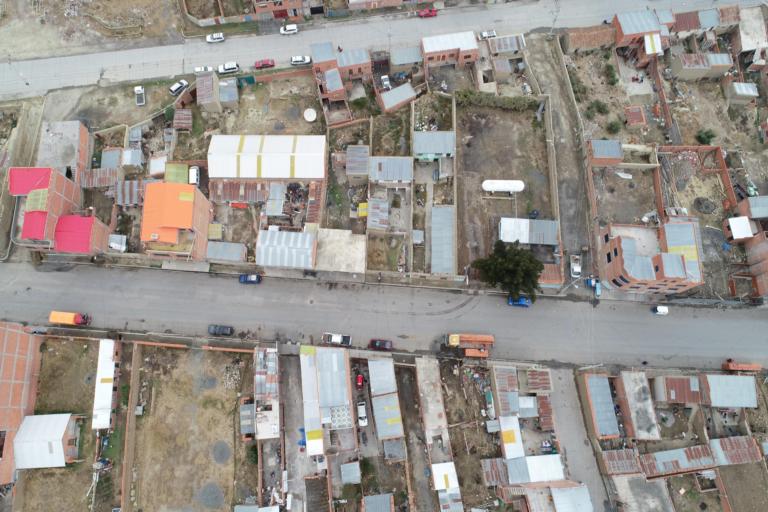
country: BO
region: La Paz
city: Achacachi
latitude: -16.0505
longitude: -68.6813
